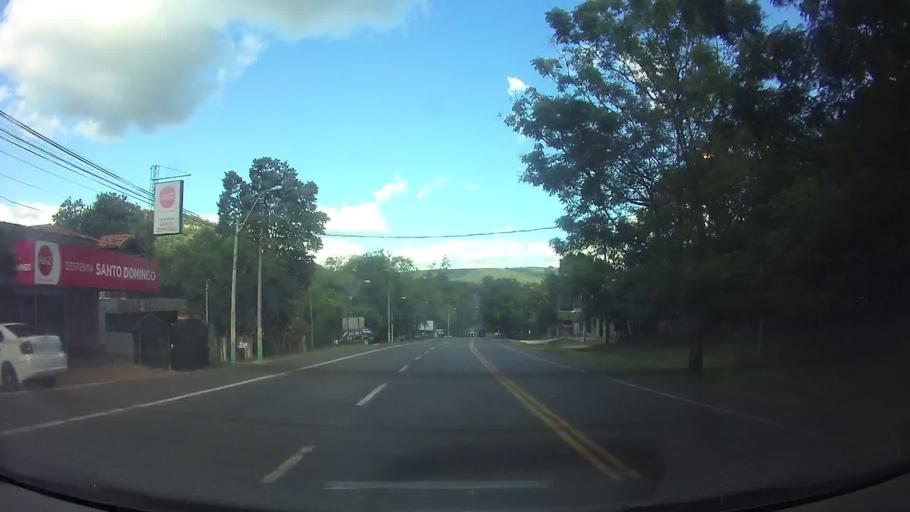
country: PY
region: Cordillera
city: Caacupe
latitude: -25.3843
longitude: -57.1262
